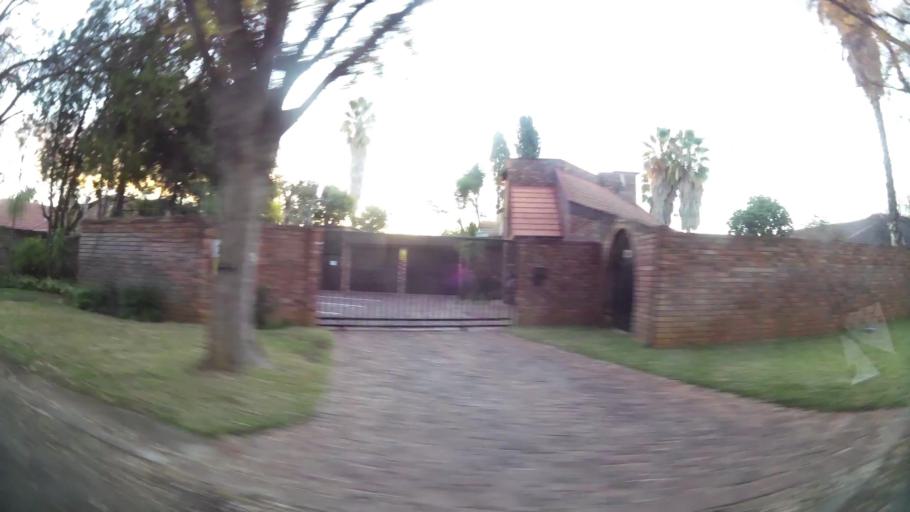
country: ZA
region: North-West
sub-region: Dr Kenneth Kaunda District Municipality
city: Potchefstroom
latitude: -26.7242
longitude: 27.1103
